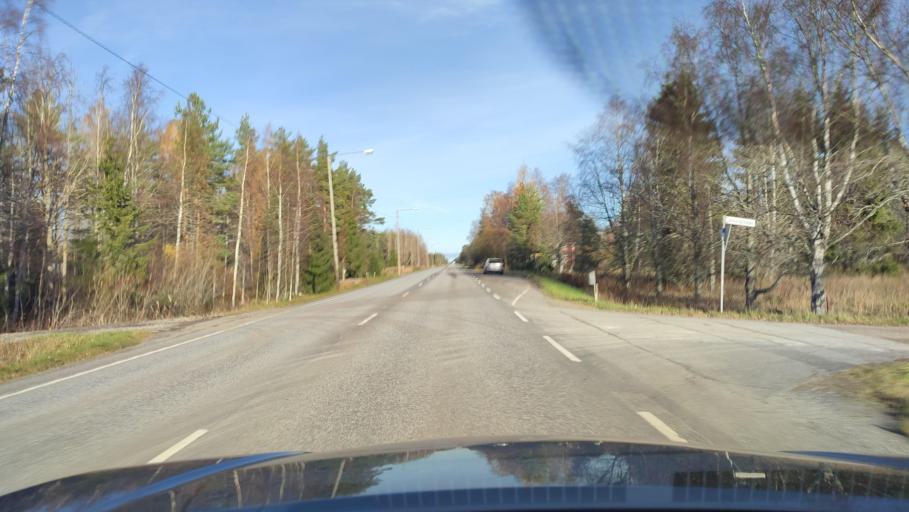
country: FI
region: Ostrobothnia
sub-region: Vaasa
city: Malax
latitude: 62.7775
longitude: 21.6622
